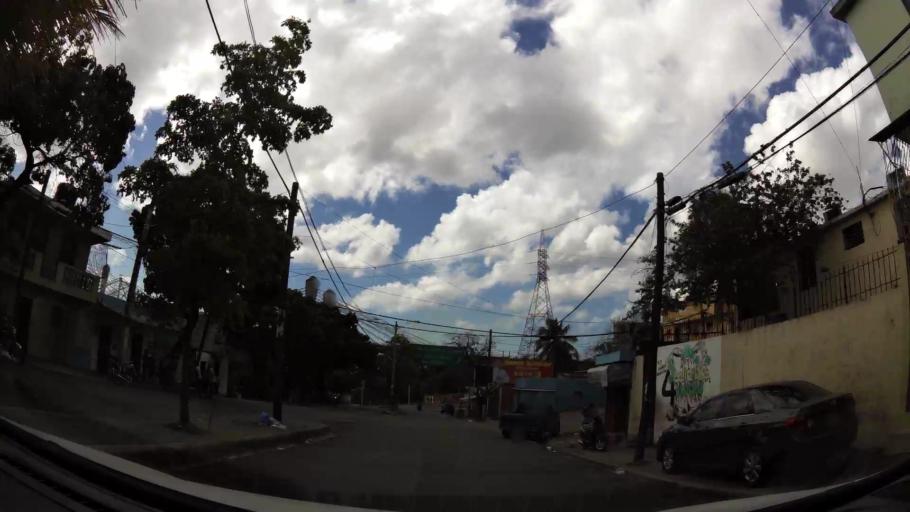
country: DO
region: Nacional
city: San Carlos
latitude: 18.4888
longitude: -69.8839
